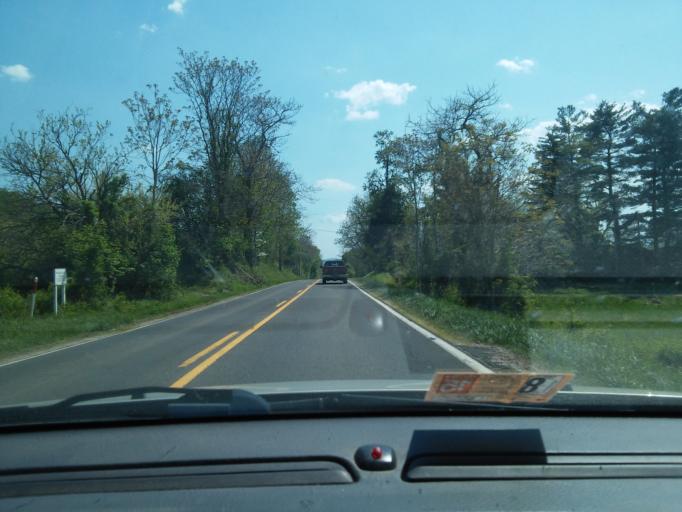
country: US
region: Virginia
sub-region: Rappahannock County
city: Washington
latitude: 38.7396
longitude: -78.1099
